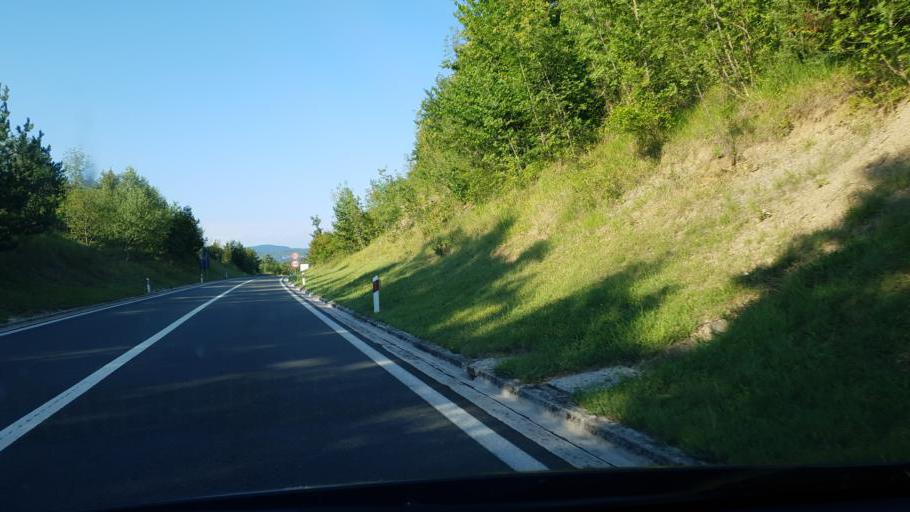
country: HR
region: Istarska
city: Buzet
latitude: 45.3153
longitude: 14.0692
